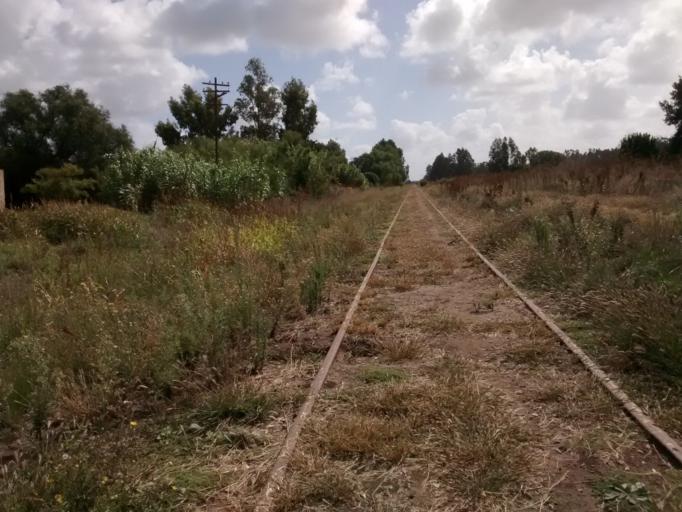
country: AR
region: Buenos Aires
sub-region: Partido de Loberia
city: Loberia
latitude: -38.1972
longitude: -58.7378
